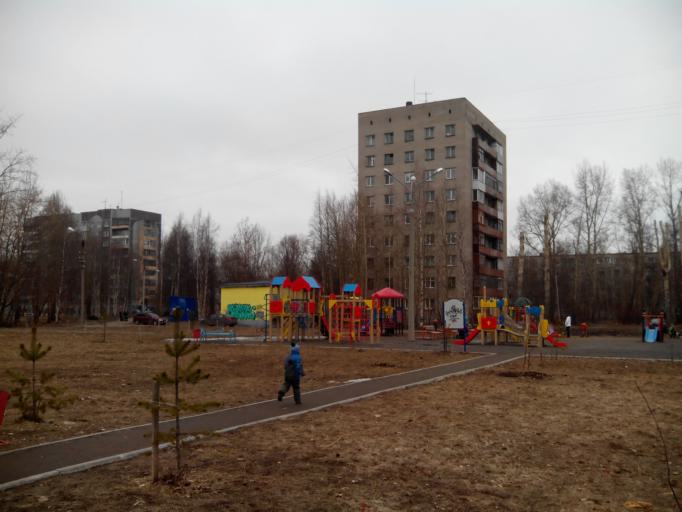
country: RU
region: Arkhangelskaya
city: Katunino
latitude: 64.5046
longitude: 40.6765
